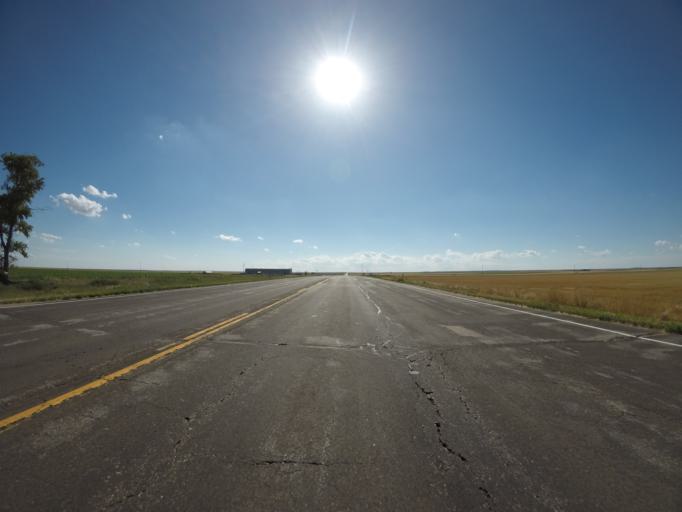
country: US
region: Colorado
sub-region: Logan County
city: Sterling
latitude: 40.6239
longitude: -103.3514
